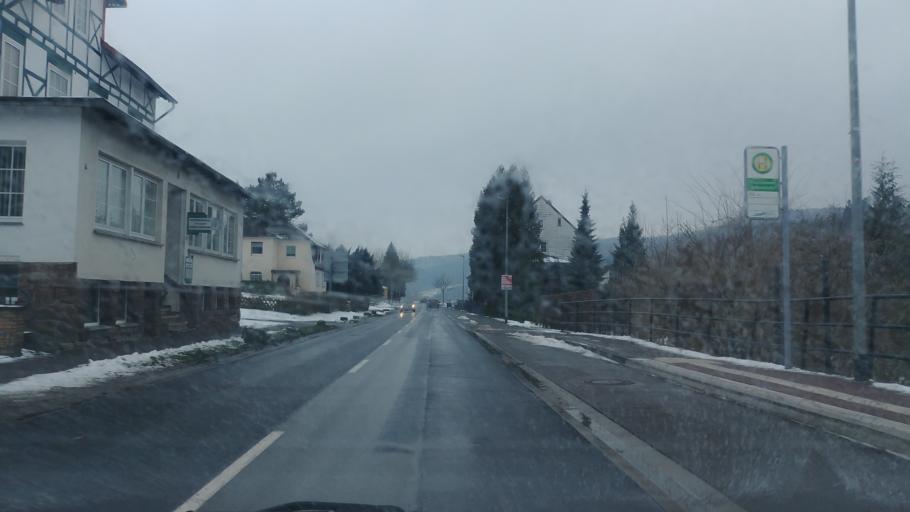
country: DE
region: Lower Saxony
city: Adelebsen
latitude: 51.6645
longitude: 9.7380
